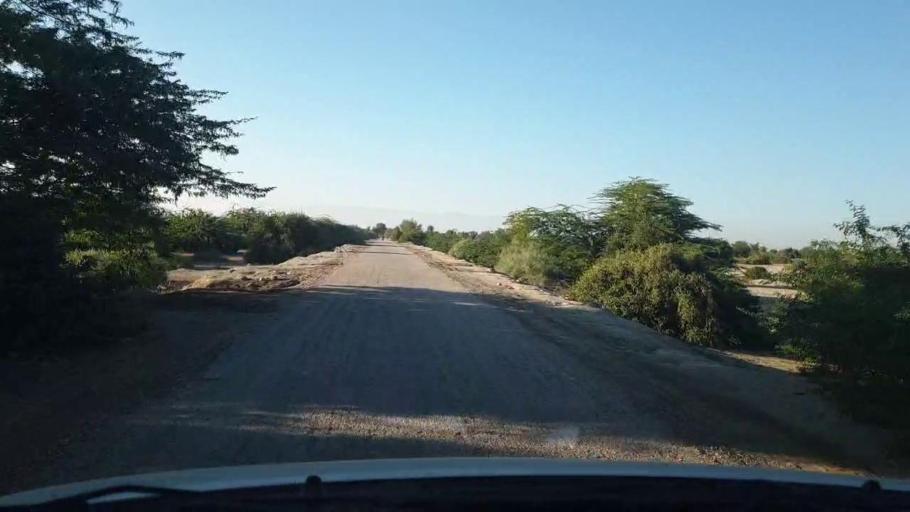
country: PK
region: Sindh
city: Johi
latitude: 26.7724
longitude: 67.4565
